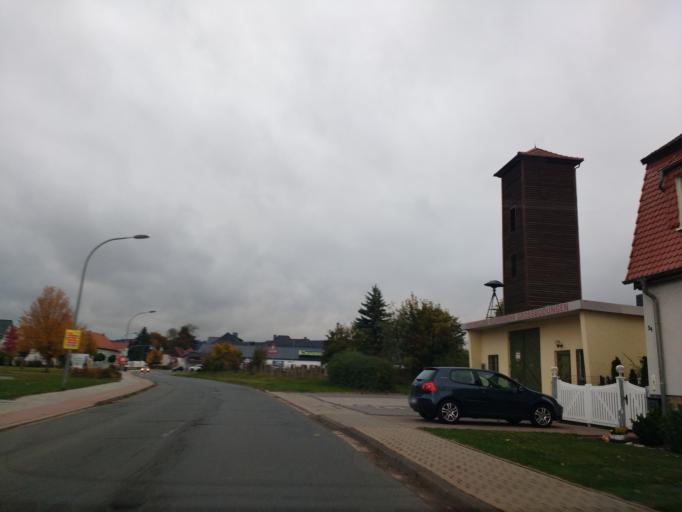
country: DE
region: Thuringia
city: Grossbodungen
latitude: 51.4776
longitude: 10.4845
